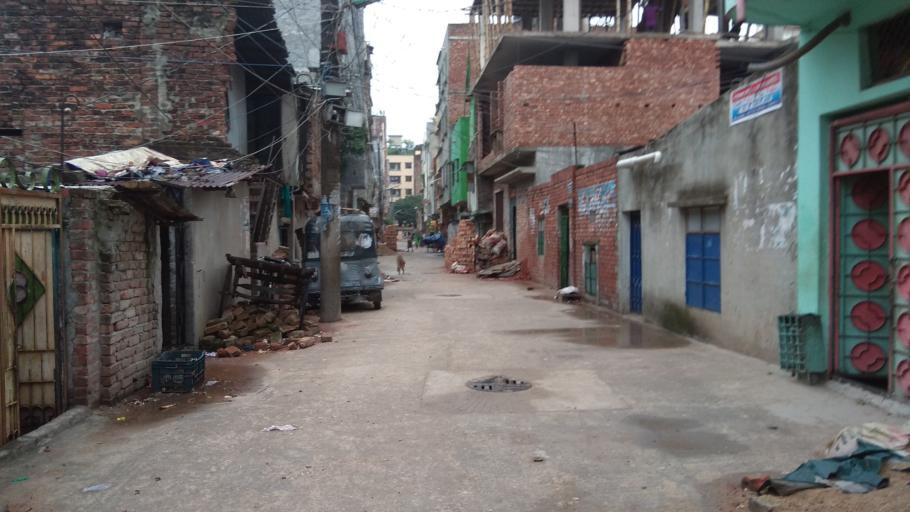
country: BD
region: Dhaka
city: Tungi
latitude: 23.8229
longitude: 90.3695
